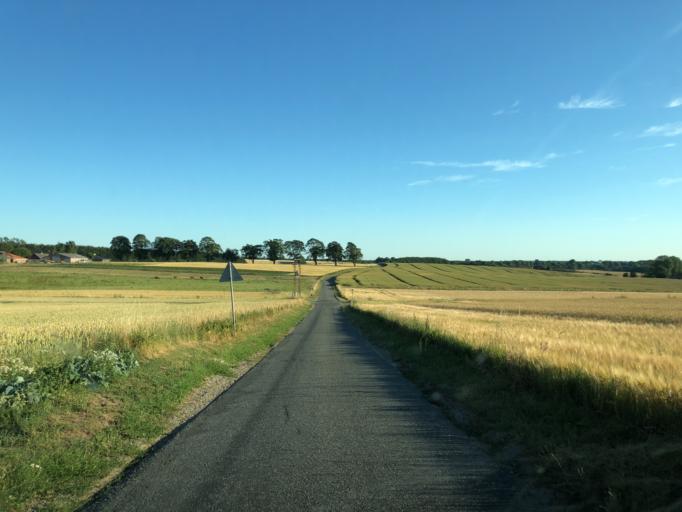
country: DK
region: Central Jutland
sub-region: Horsens Kommune
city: Horsens
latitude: 55.9041
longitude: 9.8641
